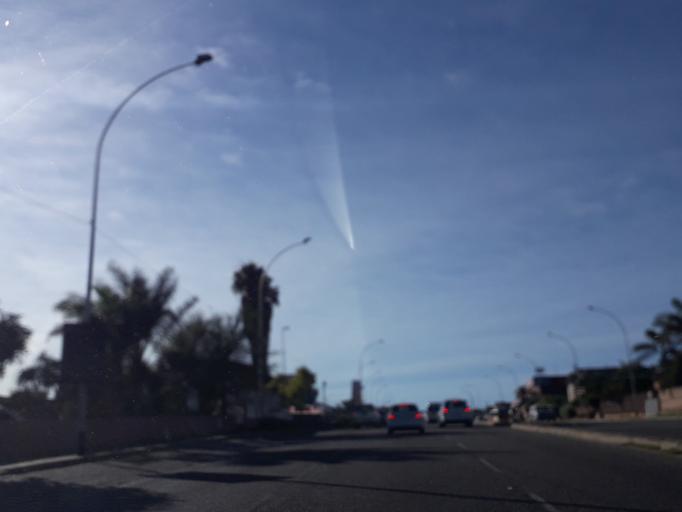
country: ZA
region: Gauteng
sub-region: City of Johannesburg Metropolitan Municipality
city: Roodepoort
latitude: -26.1655
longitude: 27.9368
